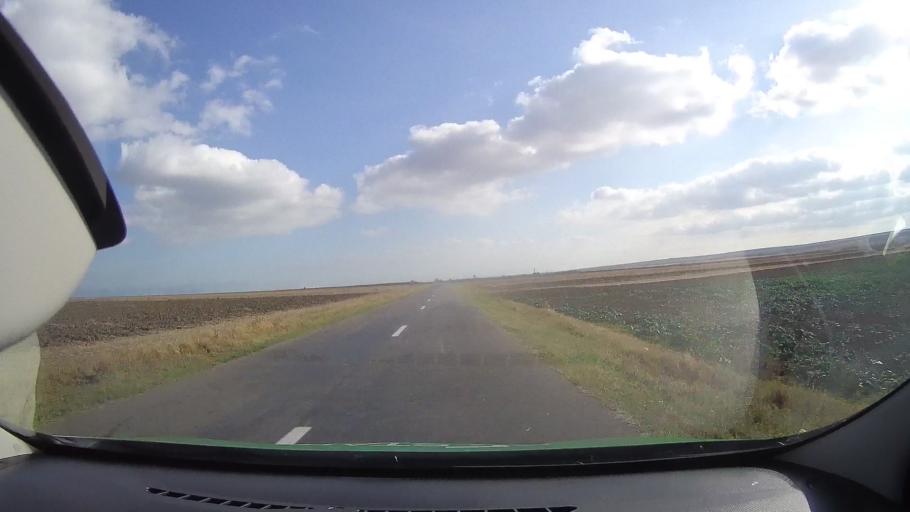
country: RO
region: Constanta
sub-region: Comuna Cogealac
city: Tariverde
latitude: 44.5565
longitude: 28.6162
